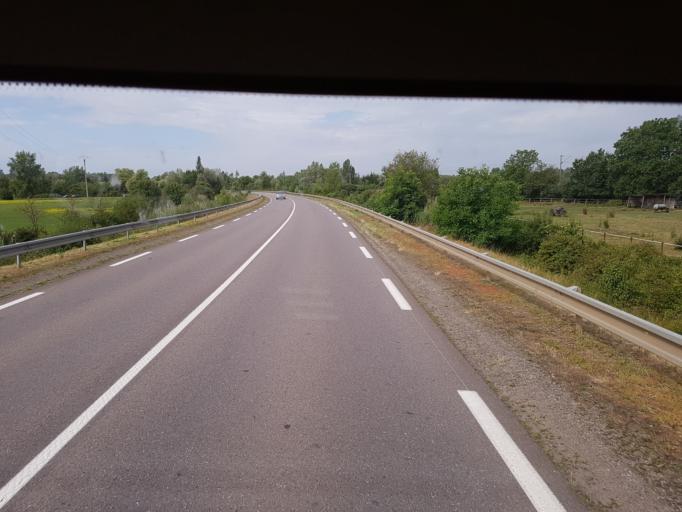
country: FR
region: Lorraine
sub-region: Departement de la Moselle
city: Koenigsmacker
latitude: 49.4056
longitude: 6.2893
